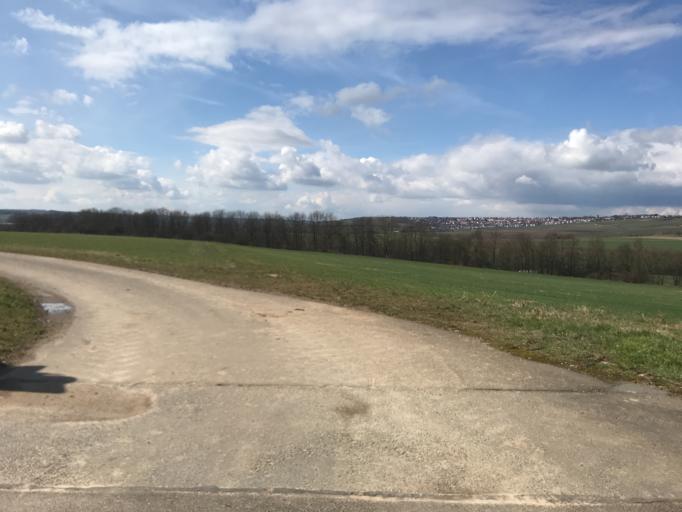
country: DE
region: Rheinland-Pfalz
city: Klein-Winternheim
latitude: 49.9276
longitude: 8.2011
